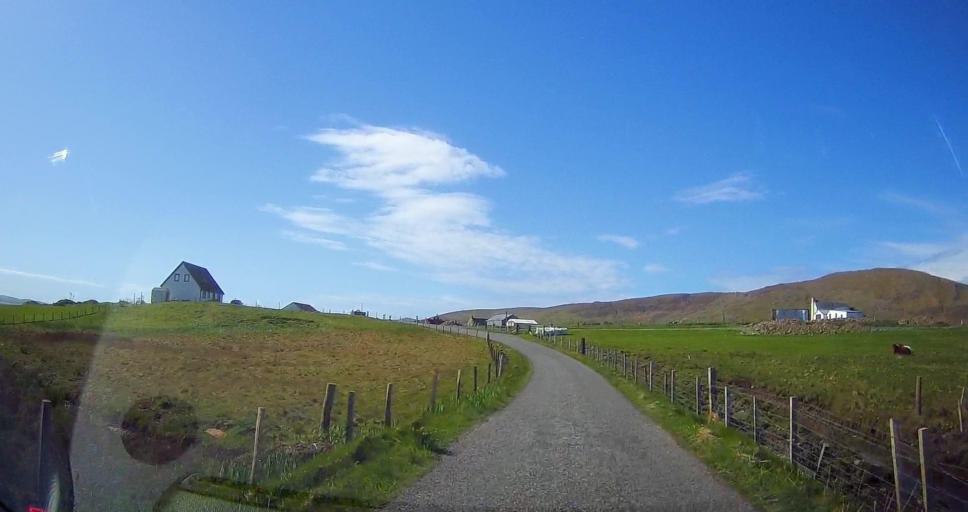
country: GB
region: Scotland
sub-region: Shetland Islands
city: Sandwick
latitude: 60.0417
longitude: -1.2177
